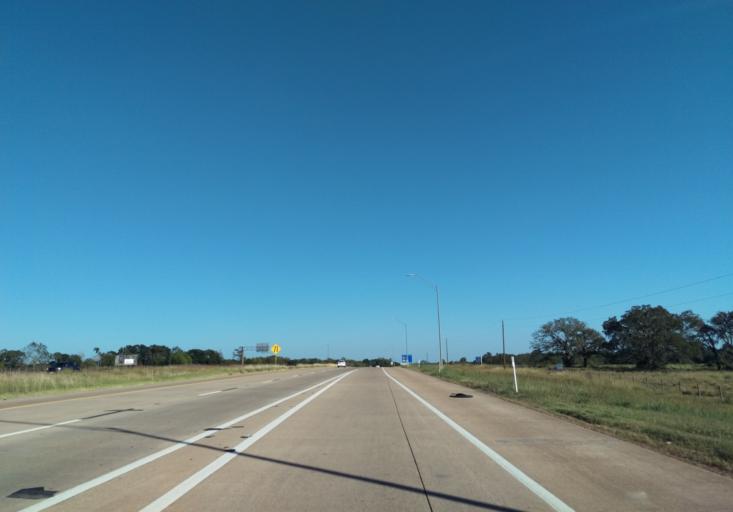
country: US
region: Texas
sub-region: Waller County
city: Hempstead
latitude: 30.1129
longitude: -96.0639
